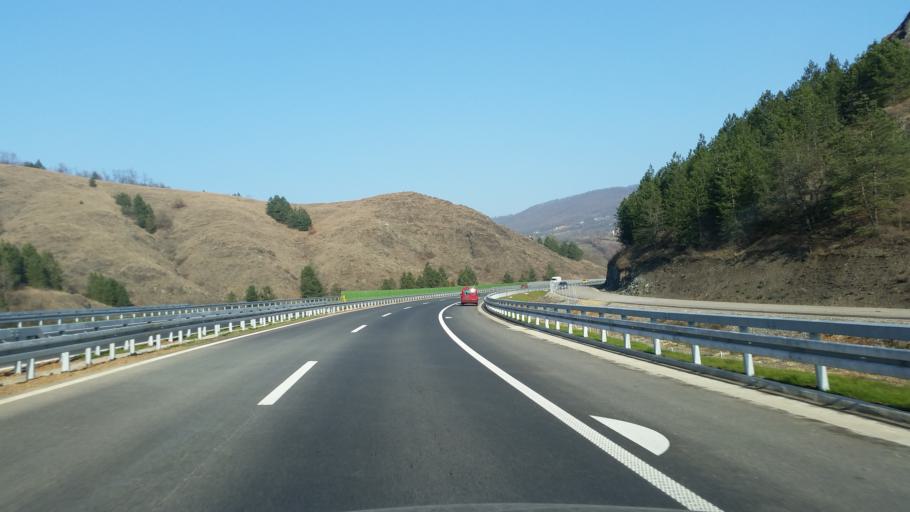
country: RS
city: Prislonica
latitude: 43.9914
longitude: 20.3994
